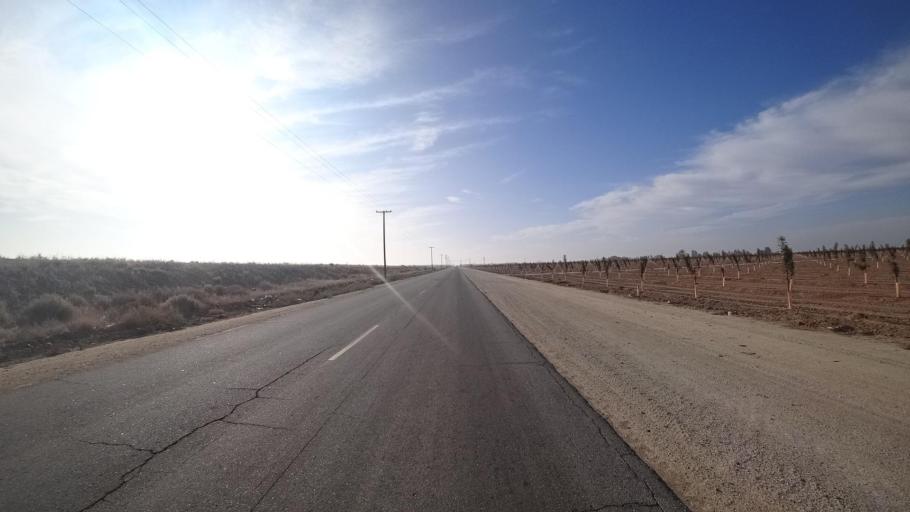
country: US
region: California
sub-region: Kern County
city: McFarland
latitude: 35.6499
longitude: -119.2046
